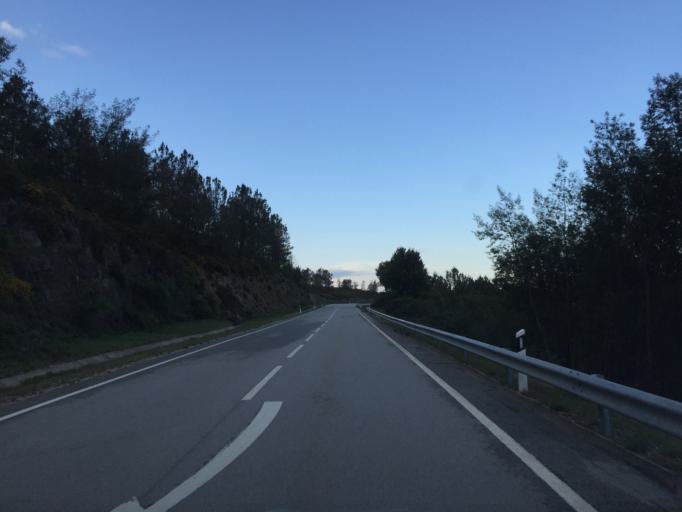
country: PT
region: Coimbra
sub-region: Gois
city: Gois
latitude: 40.1084
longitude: -8.0355
